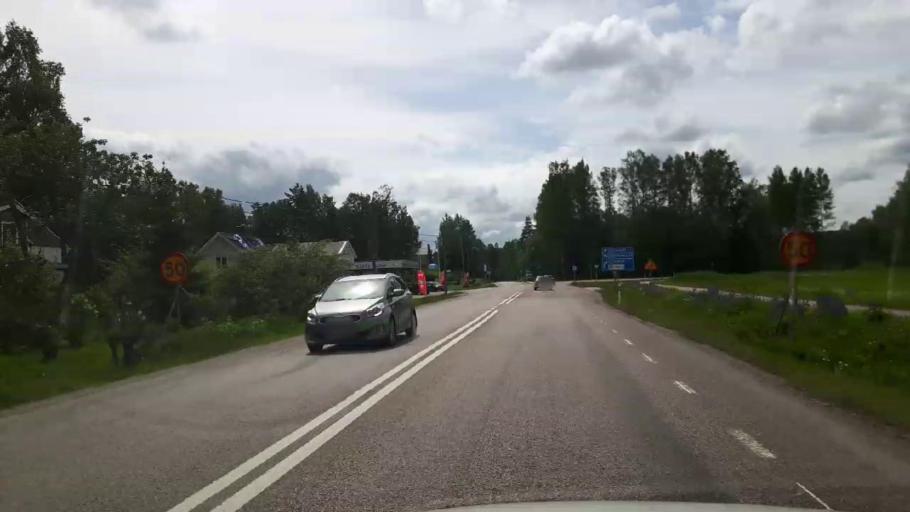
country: SE
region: Vaestmanland
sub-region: Fagersta Kommun
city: Fagersta
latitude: 59.9657
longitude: 15.7671
